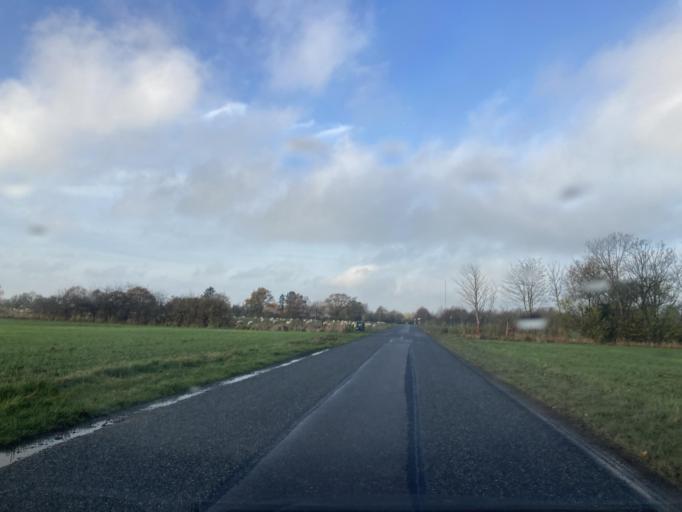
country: DK
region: Zealand
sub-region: Lolland Kommune
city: Rodby
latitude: 54.6877
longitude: 11.3961
